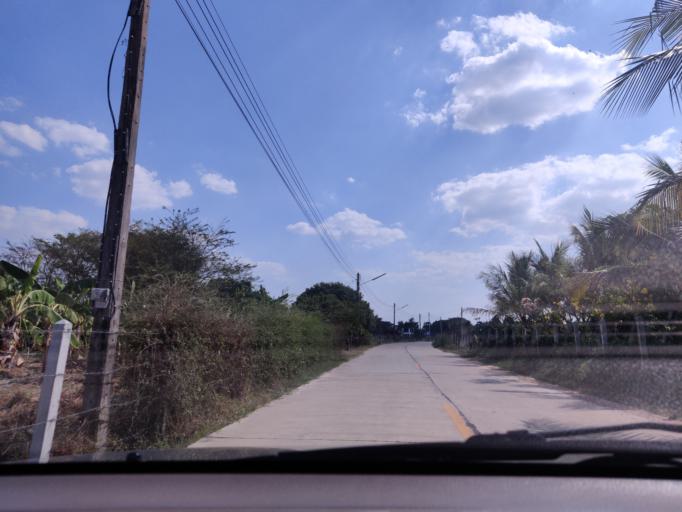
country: TH
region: Sisaket
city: Si Sa Ket
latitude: 15.0991
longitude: 104.3554
